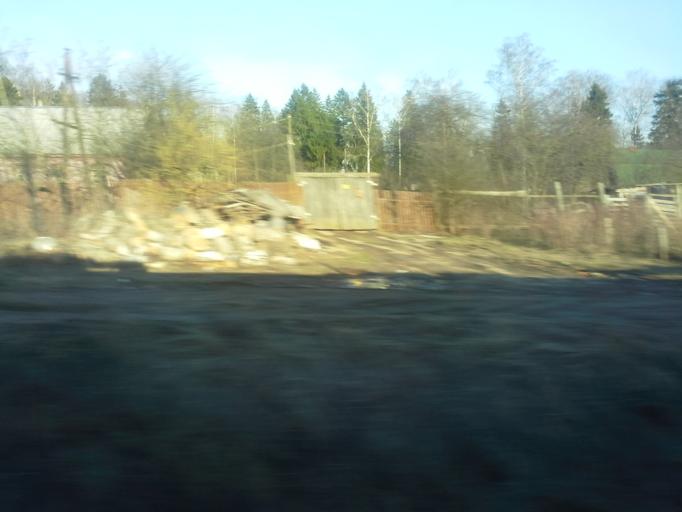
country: RU
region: Moskovskaya
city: Nekrasovskiy
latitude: 56.0967
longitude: 37.5075
